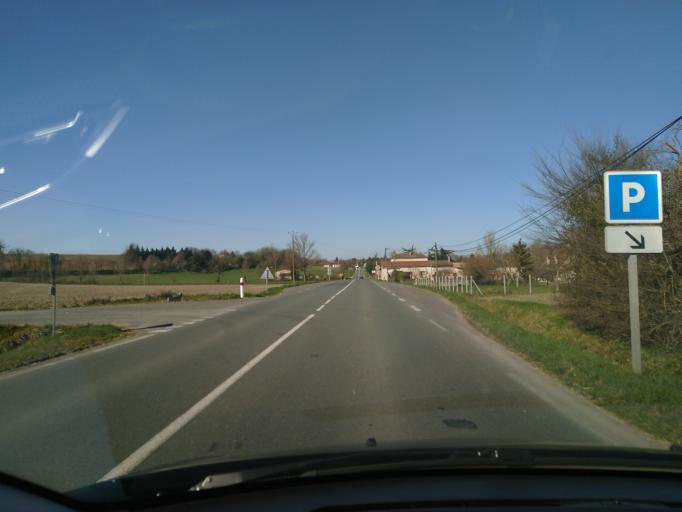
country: FR
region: Aquitaine
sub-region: Departement de la Dordogne
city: Monbazillac
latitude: 44.7505
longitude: 0.5346
